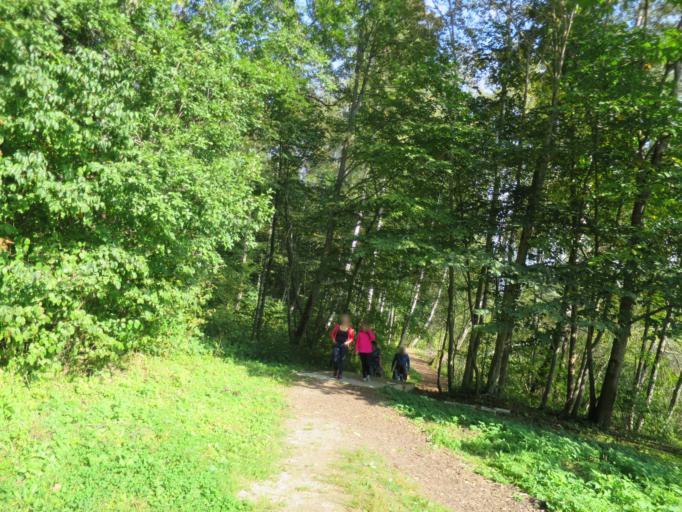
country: LV
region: Sigulda
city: Sigulda
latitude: 57.1498
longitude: 24.8069
